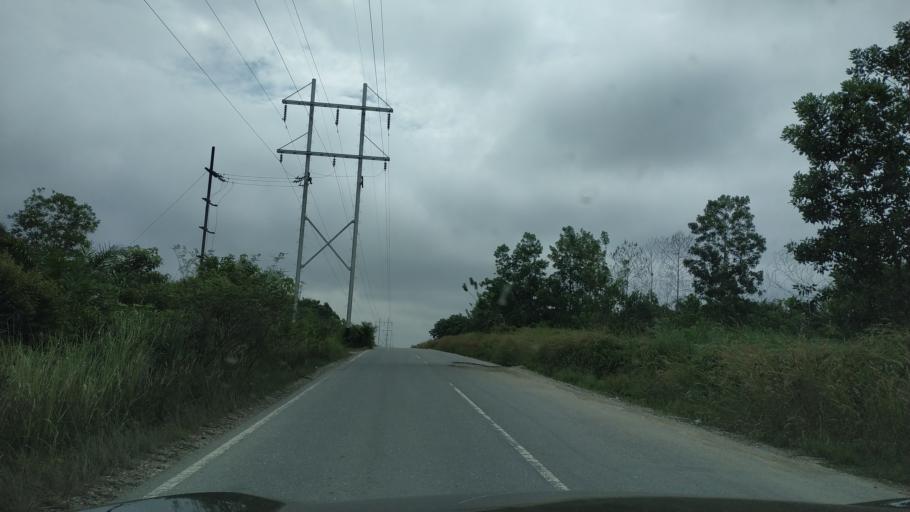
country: ID
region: Riau
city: Pekanbaru
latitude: 0.6435
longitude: 101.6754
